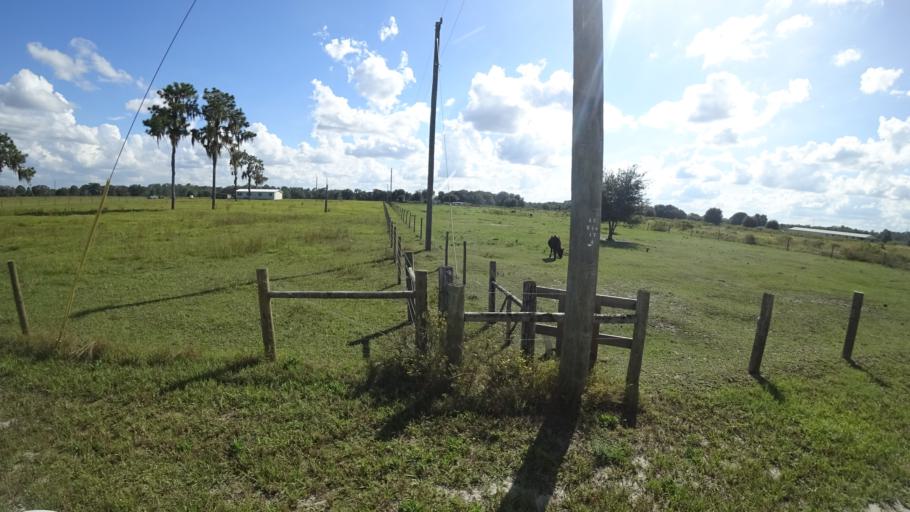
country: US
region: Florida
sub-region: Hardee County
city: Wauchula
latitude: 27.4897
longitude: -82.0676
